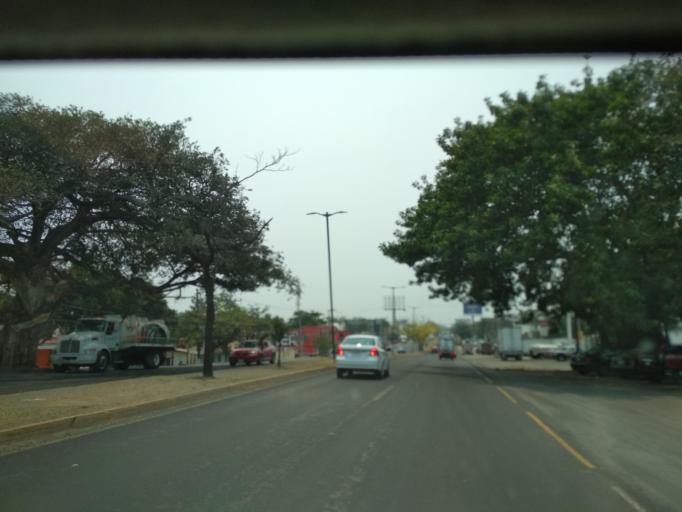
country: MX
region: Veracruz
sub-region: Veracruz
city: Las Amapolas
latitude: 19.1663
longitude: -96.2167
